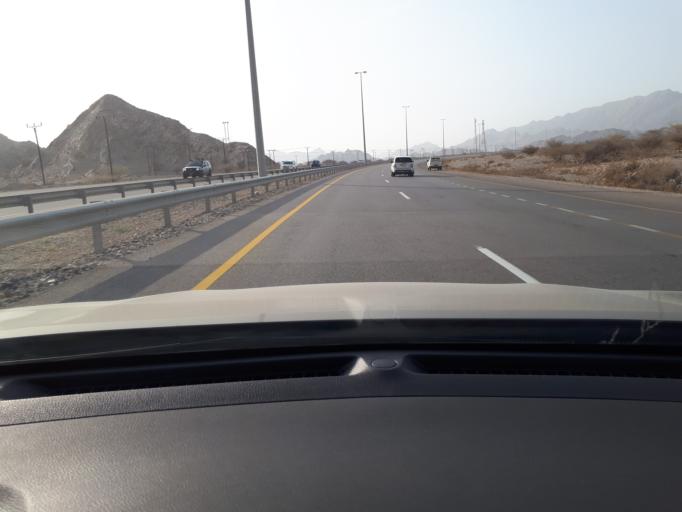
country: OM
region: Muhafazat Masqat
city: Muscat
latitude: 23.2880
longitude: 58.7440
